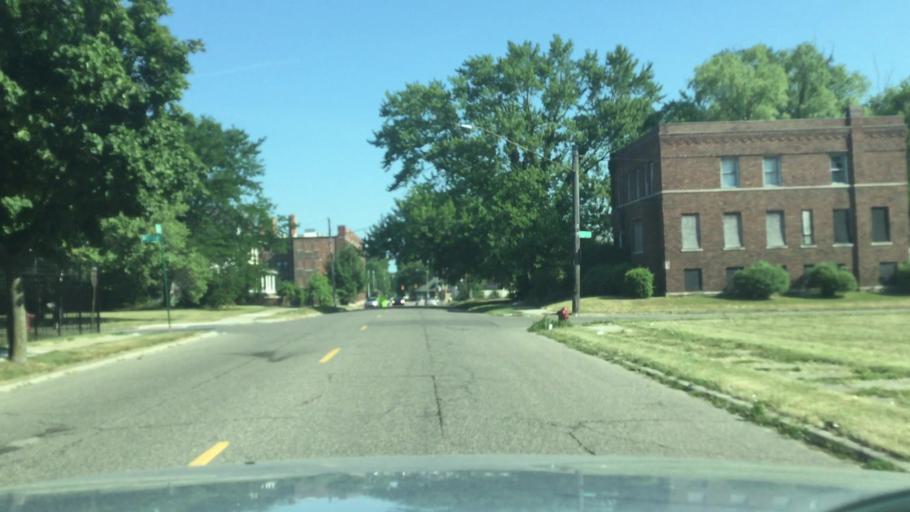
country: US
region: Michigan
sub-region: Wayne County
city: Grosse Pointe Park
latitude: 42.3607
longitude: -82.9860
